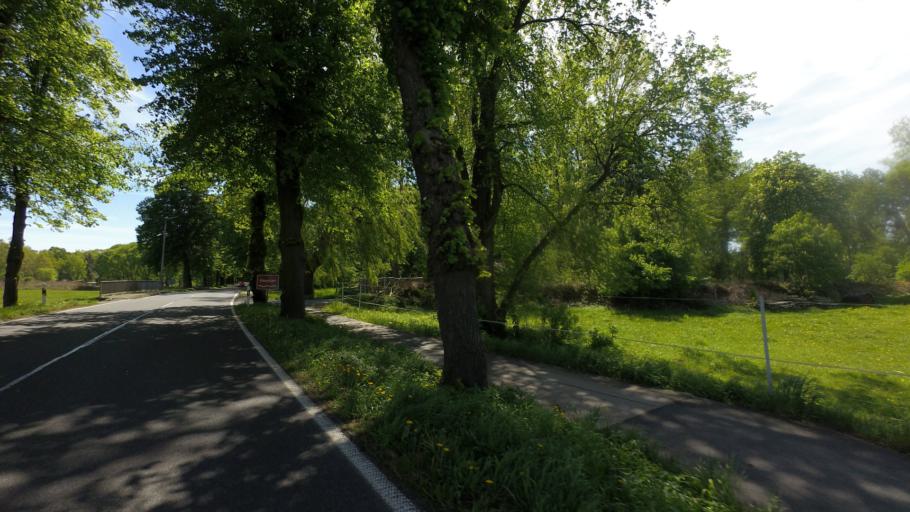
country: DE
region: Brandenburg
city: Luckenwalde
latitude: 52.0755
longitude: 13.1859
